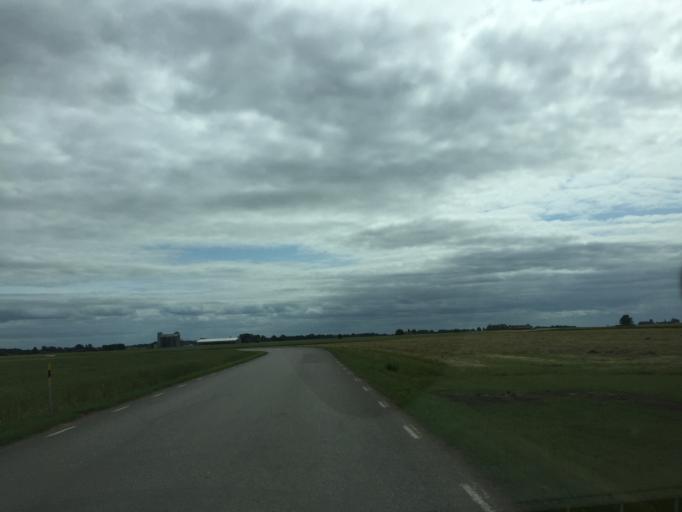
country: SE
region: OEstergoetland
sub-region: Vadstena Kommun
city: Vadstena
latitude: 58.4419
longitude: 14.8442
